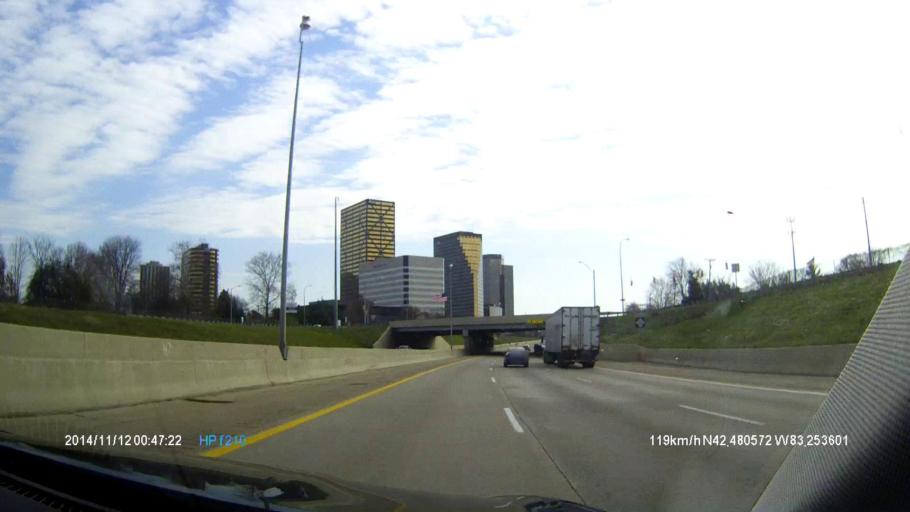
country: US
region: Michigan
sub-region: Oakland County
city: Southfield
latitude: 42.4804
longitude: -83.2532
